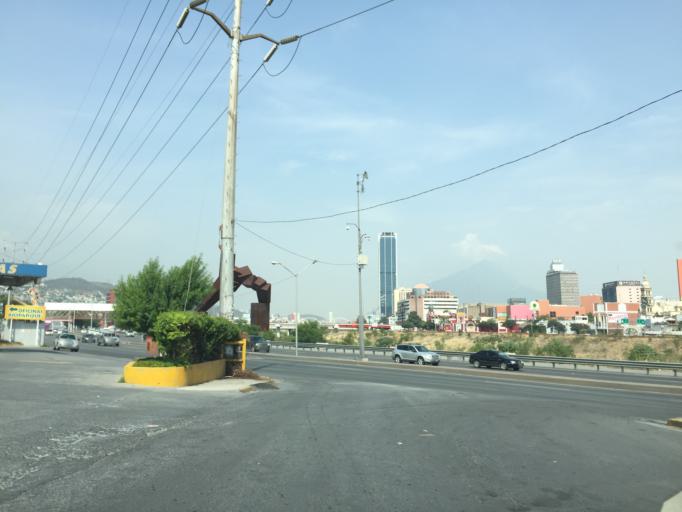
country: MX
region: Nuevo Leon
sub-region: Monterrey
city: Monterrey
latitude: 25.6624
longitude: -100.3051
